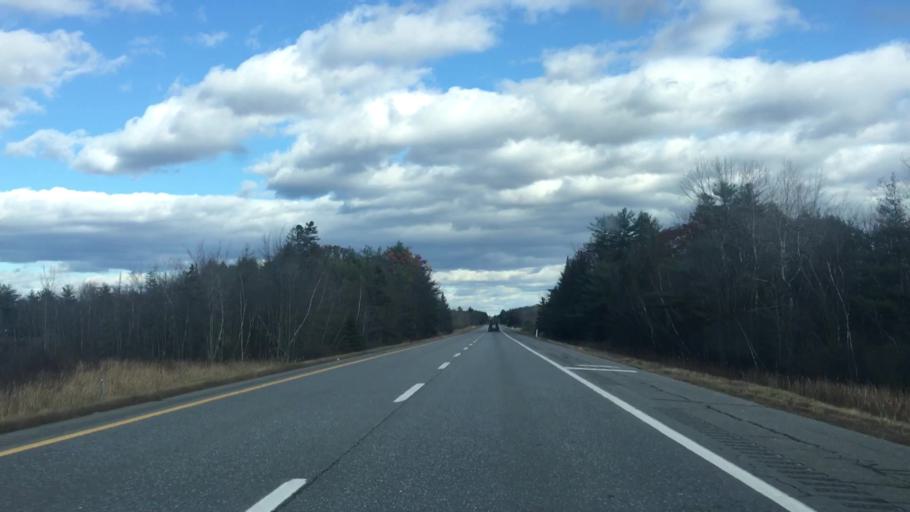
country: US
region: Maine
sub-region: Kennebec County
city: Benton
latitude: 44.6086
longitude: -69.5708
